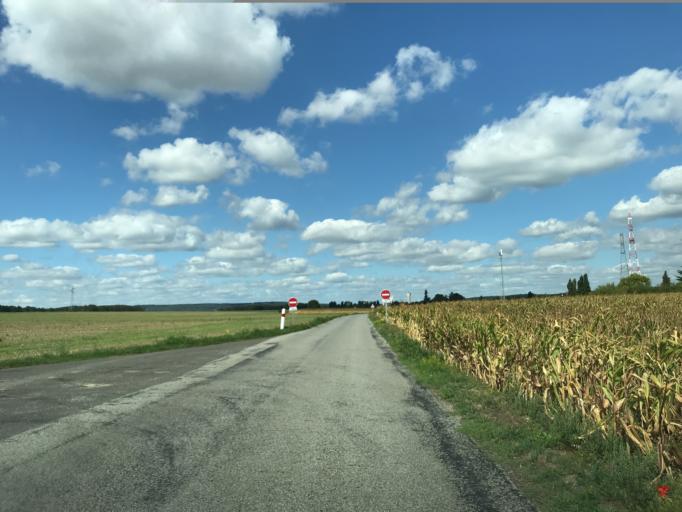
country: FR
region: Haute-Normandie
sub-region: Departement de l'Eure
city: Courcelles-sur-Seine
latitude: 49.1514
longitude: 1.4056
